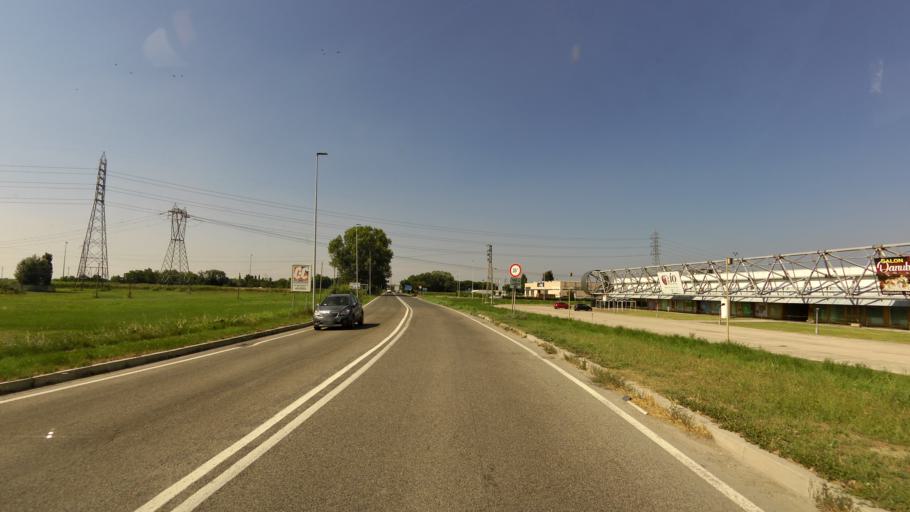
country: IT
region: Emilia-Romagna
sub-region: Provincia di Ravenna
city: Ravenna
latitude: 44.4522
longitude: 12.2096
